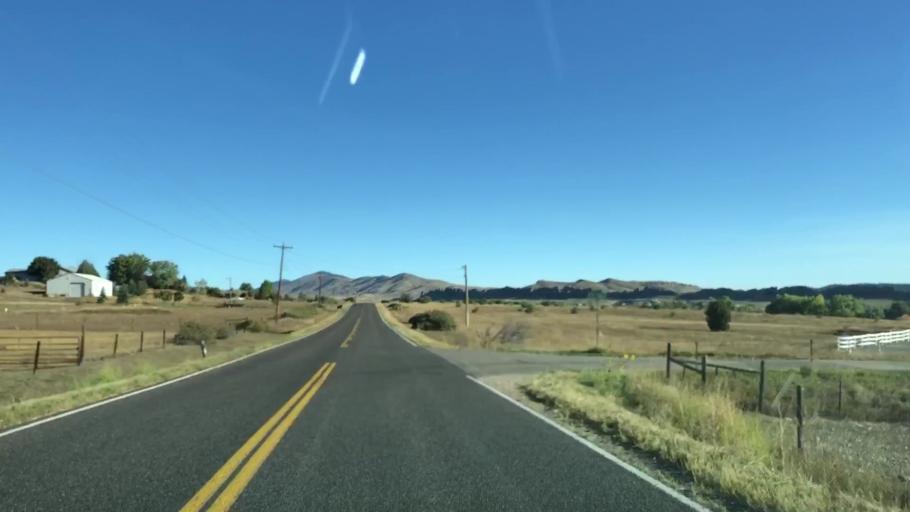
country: US
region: Colorado
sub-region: Larimer County
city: Loveland
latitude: 40.3978
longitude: -105.1684
